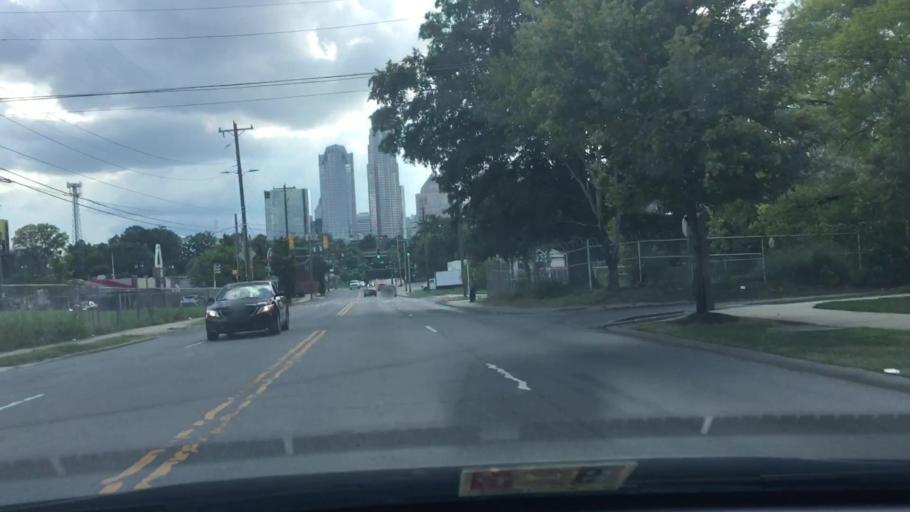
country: US
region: North Carolina
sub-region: Mecklenburg County
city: Charlotte
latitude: 35.2365
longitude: -80.8306
